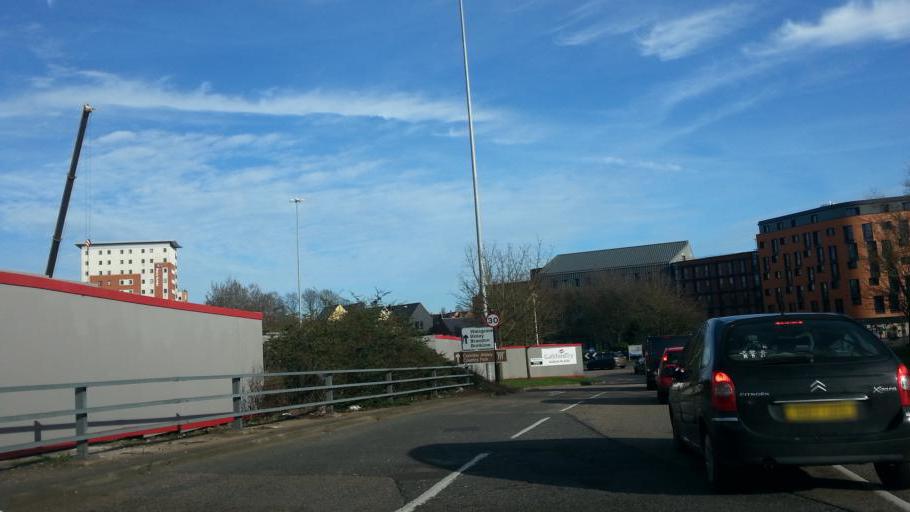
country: GB
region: England
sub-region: Coventry
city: Coventry
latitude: 52.4080
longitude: -1.5003
